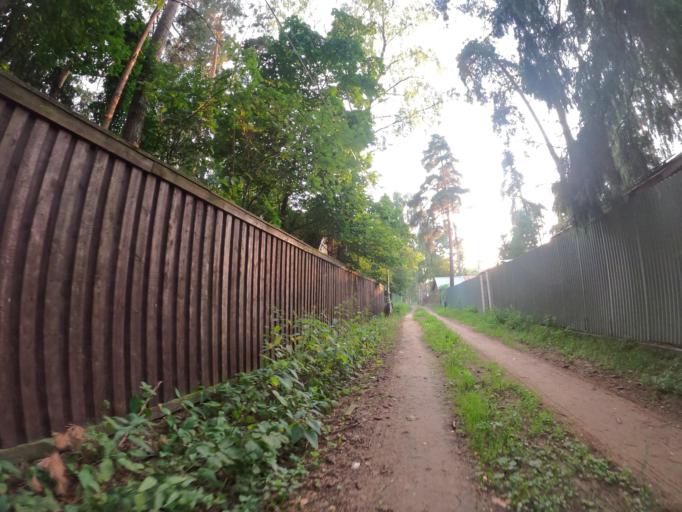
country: RU
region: Moskovskaya
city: Bykovo
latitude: 55.6344
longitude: 38.0790
